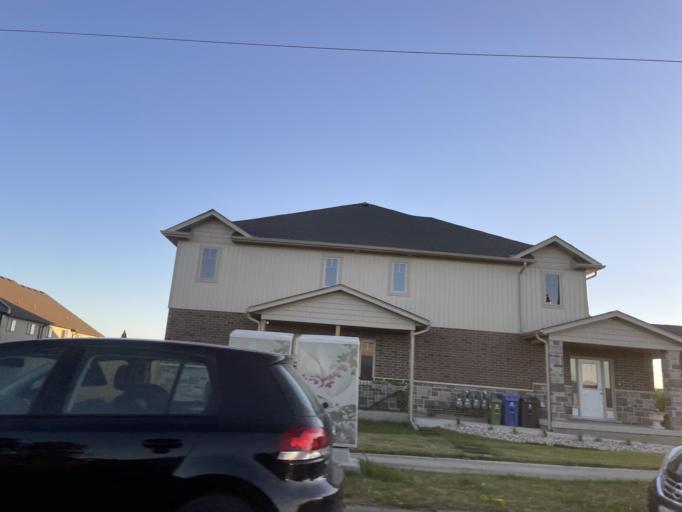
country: CA
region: Ontario
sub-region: Wellington County
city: Guelph
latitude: 43.5817
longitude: -80.2655
